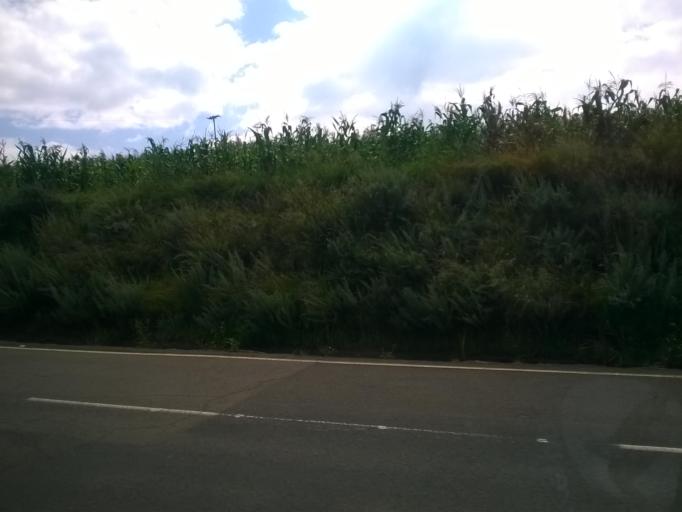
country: LS
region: Thaba-Tseka
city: Thaba-Tseka
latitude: -29.1463
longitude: 28.4913
